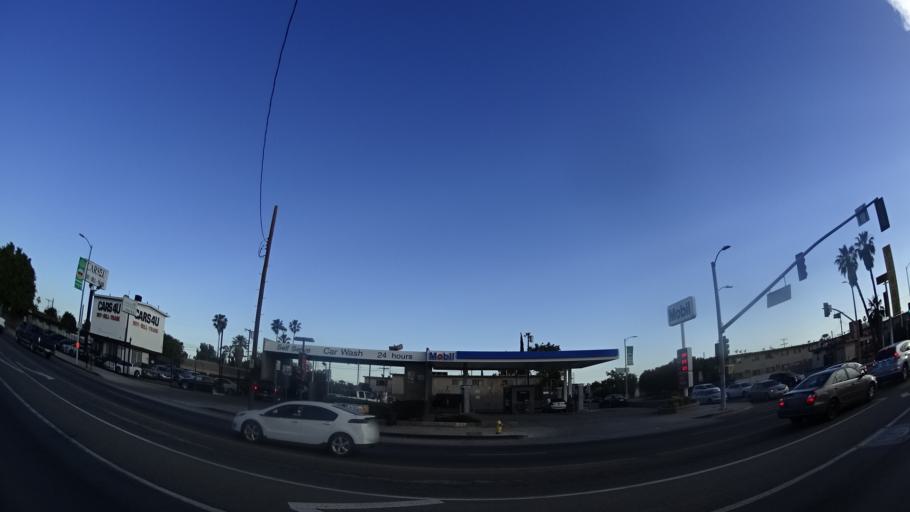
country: US
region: California
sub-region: Los Angeles County
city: North Hollywood
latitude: 34.2217
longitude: -118.4048
